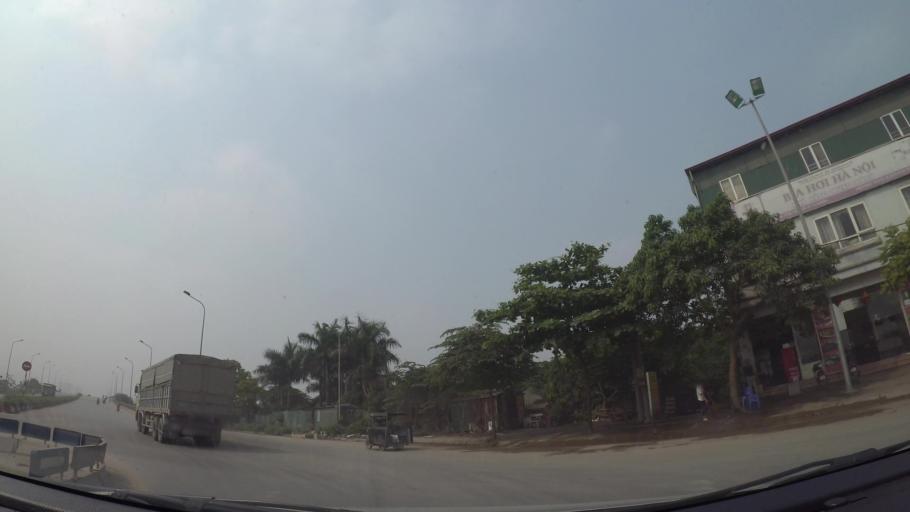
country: VN
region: Ha Noi
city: Cau Dien
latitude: 21.0118
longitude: 105.7468
